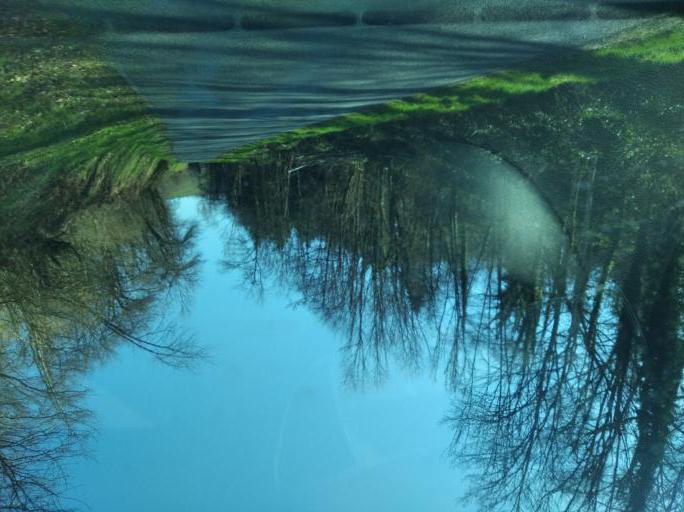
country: FR
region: Auvergne
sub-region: Departement de l'Allier
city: Le Mayet-de-Montagne
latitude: 46.0870
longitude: 3.6812
